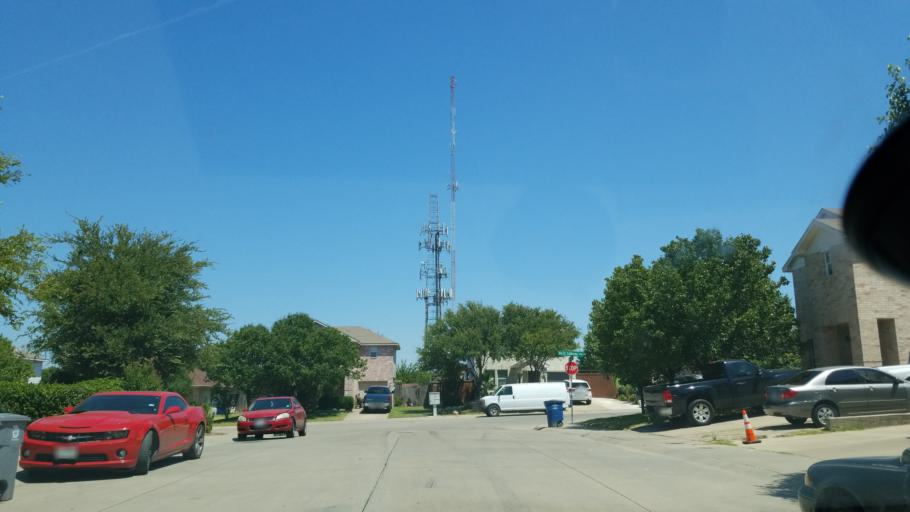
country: US
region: Texas
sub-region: Dallas County
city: Cockrell Hill
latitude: 32.7389
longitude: -96.8953
